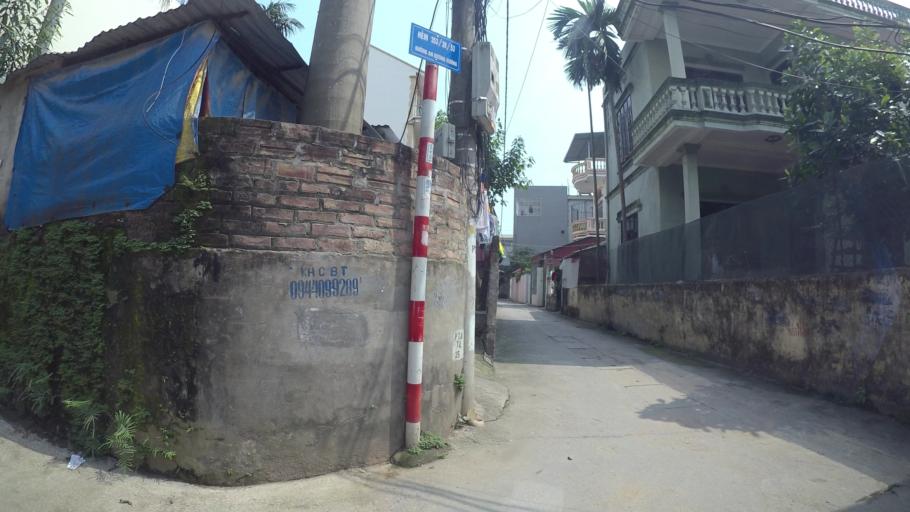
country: VN
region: Ha Noi
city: Tay Ho
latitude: 21.0872
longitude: 105.7972
